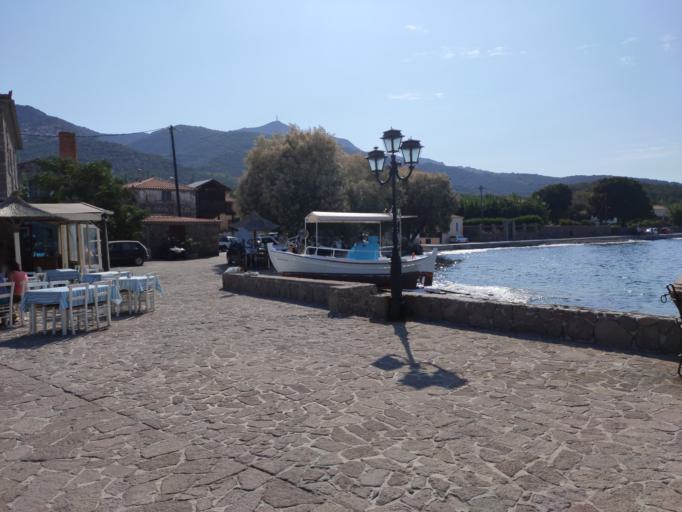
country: GR
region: North Aegean
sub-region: Nomos Lesvou
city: Mantamados
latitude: 39.3741
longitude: 26.3030
